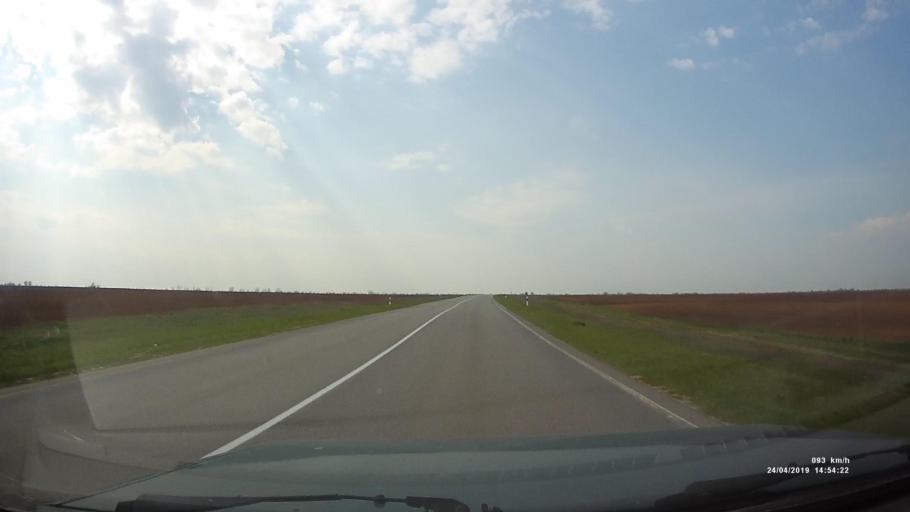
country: RU
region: Rostov
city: Remontnoye
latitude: 46.5339
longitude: 43.6400
